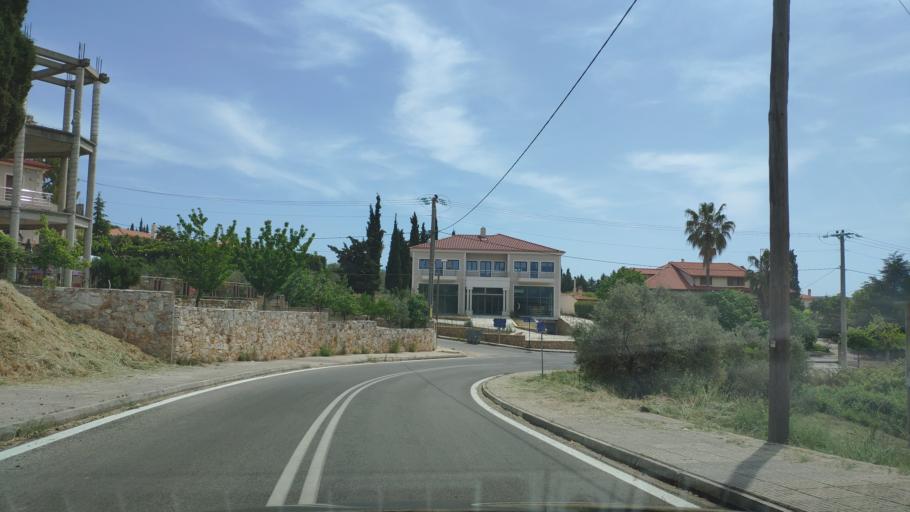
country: GR
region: Attica
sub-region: Nomarchia Anatolikis Attikis
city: Kapandriti
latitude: 38.2133
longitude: 23.8809
